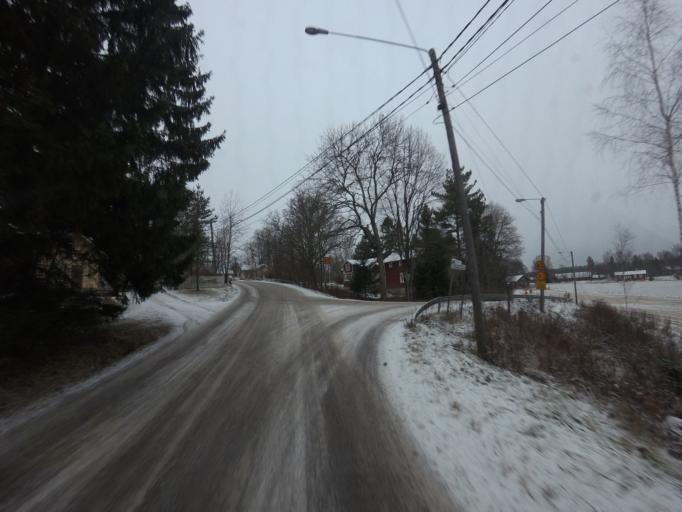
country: FI
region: Uusimaa
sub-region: Helsinki
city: Espoo
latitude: 60.1990
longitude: 24.5588
